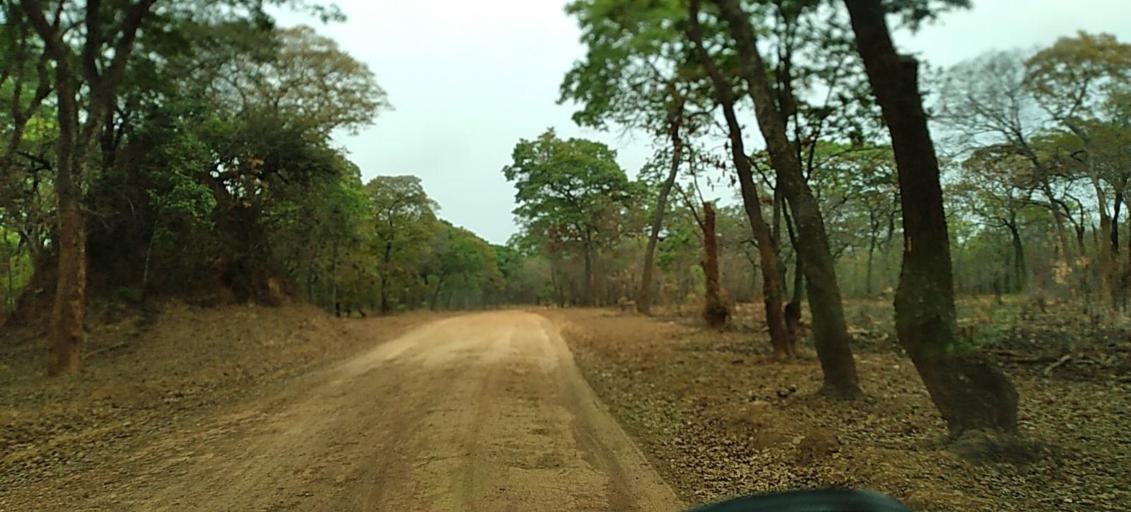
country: ZM
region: North-Western
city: Solwezi
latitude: -12.9143
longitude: 26.5570
